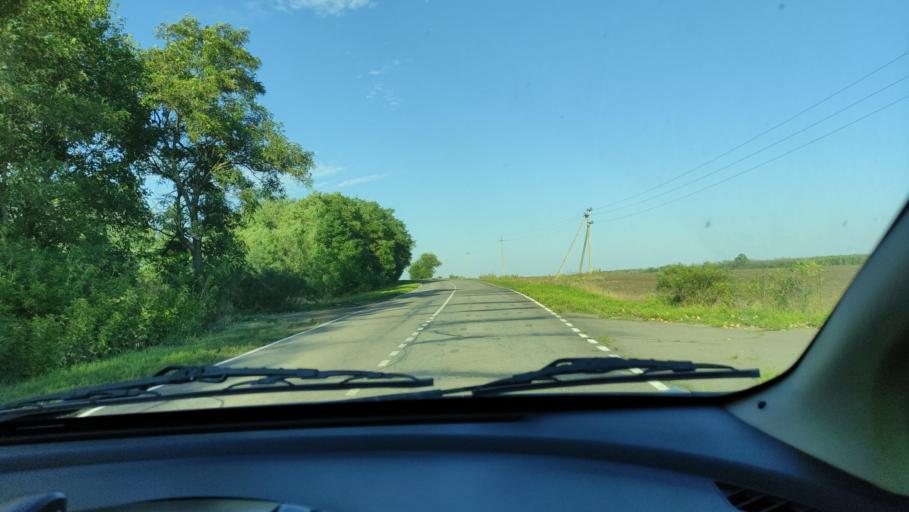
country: RU
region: Voronezj
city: Verkhniy Mamon
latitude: 50.1231
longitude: 40.3087
